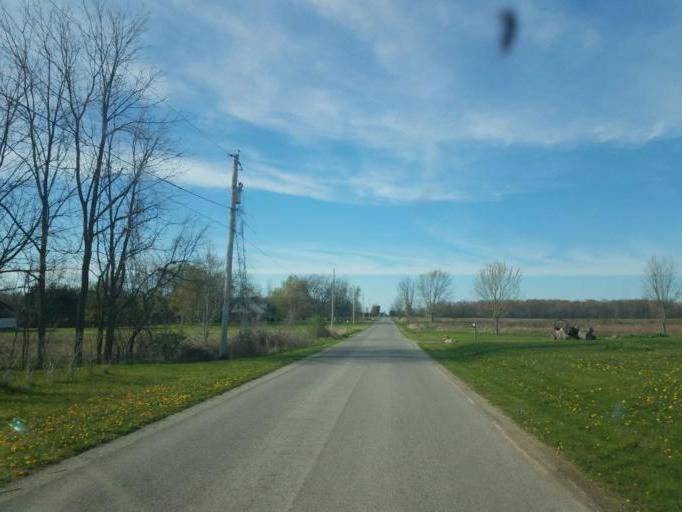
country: US
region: Ohio
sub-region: Crawford County
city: Galion
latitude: 40.6403
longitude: -82.7849
